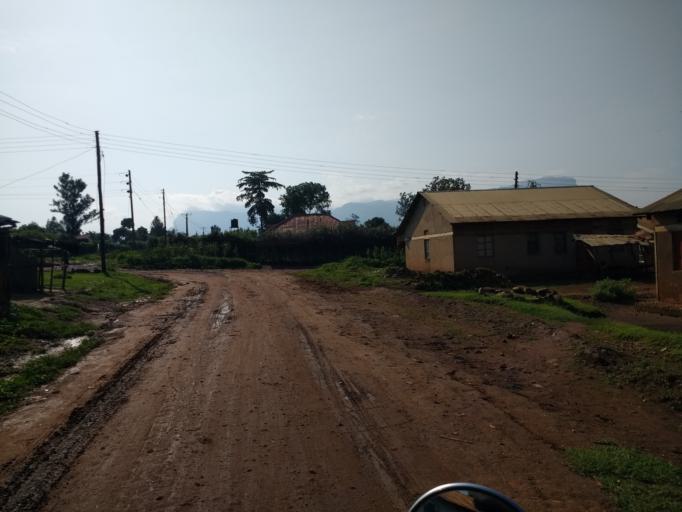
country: UG
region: Eastern Region
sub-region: Mbale District
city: Mbale
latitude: 1.0666
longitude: 34.1636
